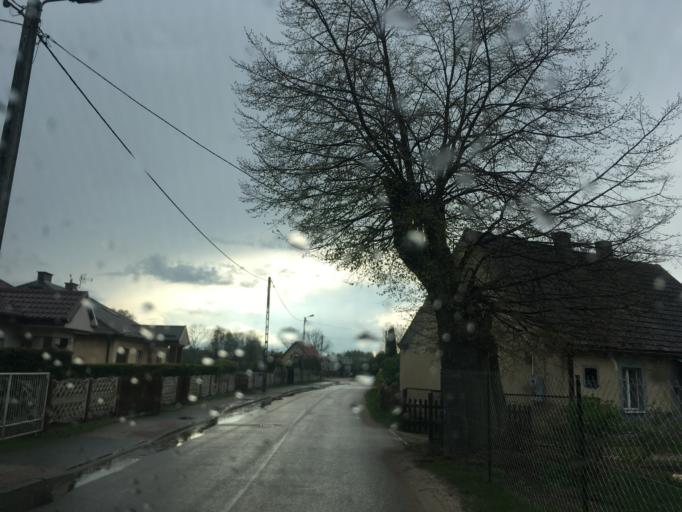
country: PL
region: Warmian-Masurian Voivodeship
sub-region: Powiat dzialdowski
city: Rybno
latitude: 53.3796
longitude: 19.9414
